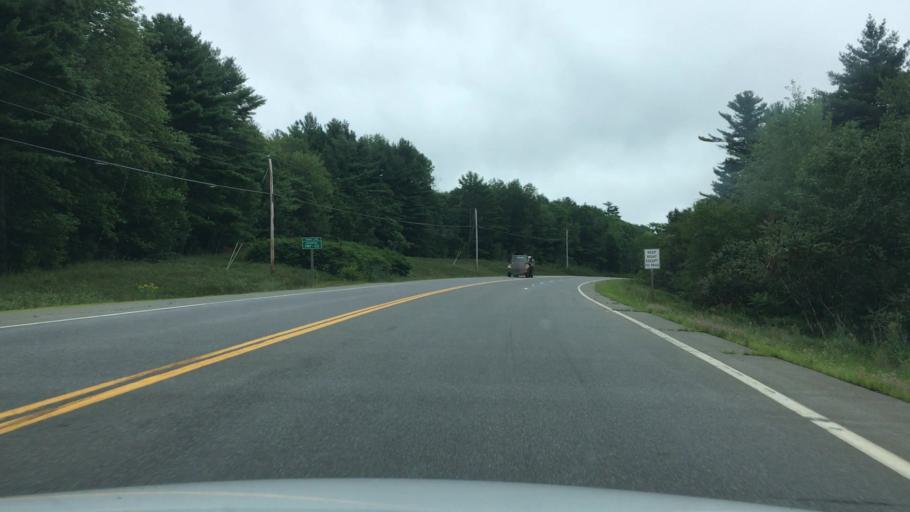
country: US
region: Maine
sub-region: Hancock County
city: Franklin
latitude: 44.8403
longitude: -68.1513
